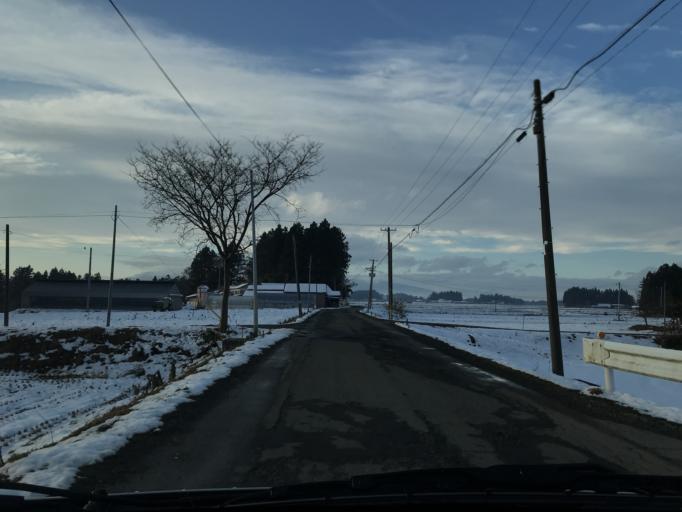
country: JP
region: Iwate
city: Mizusawa
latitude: 39.0550
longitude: 141.0943
